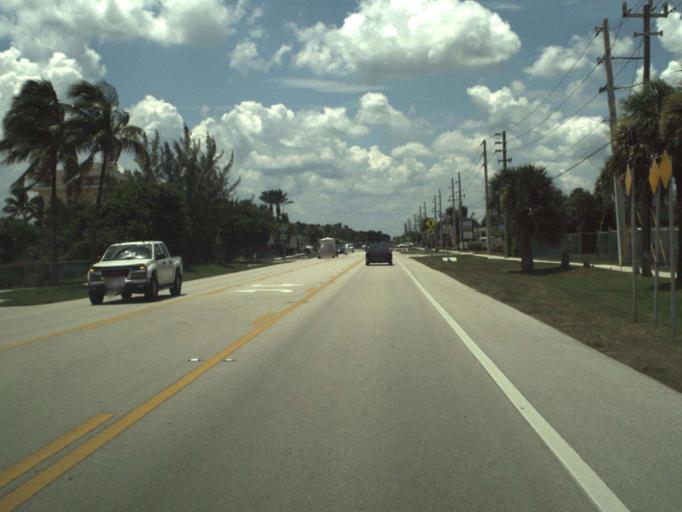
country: US
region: Florida
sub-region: Martin County
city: Jensen Beach
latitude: 27.2673
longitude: -80.2034
